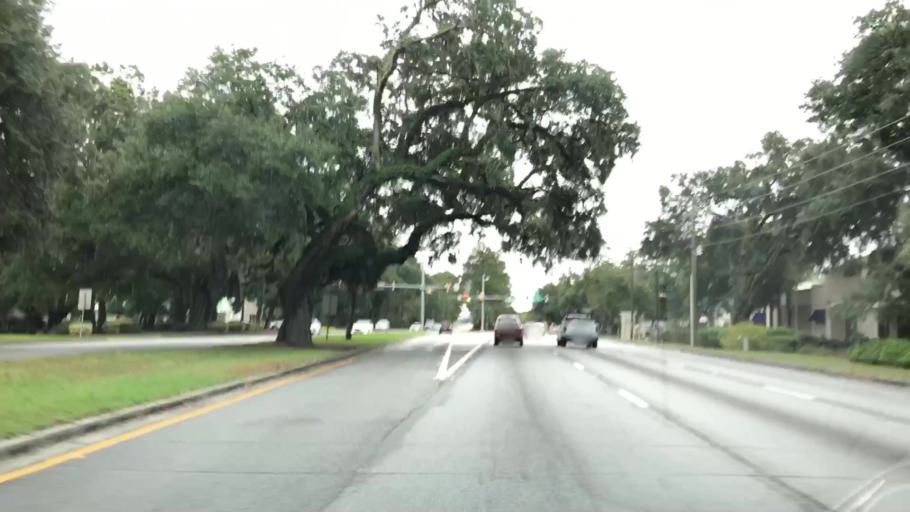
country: US
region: South Carolina
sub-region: Beaufort County
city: Bluffton
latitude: 32.2382
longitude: -80.8110
